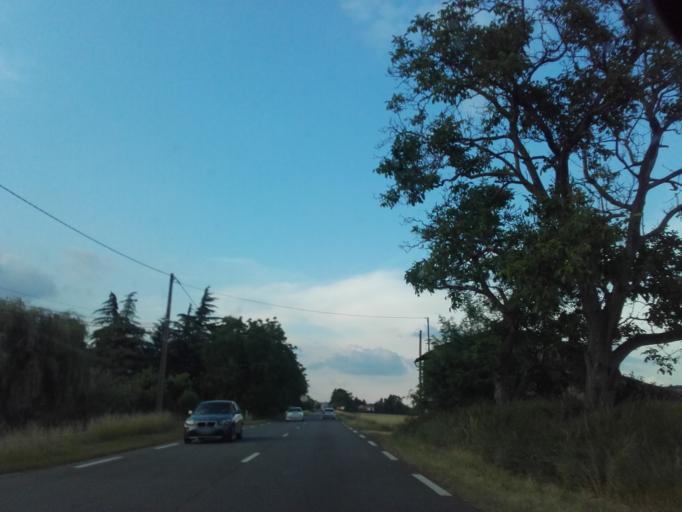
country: FR
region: Rhone-Alpes
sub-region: Departement de l'Isere
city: Reventin-Vaugris
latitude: 45.4649
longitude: 4.8268
